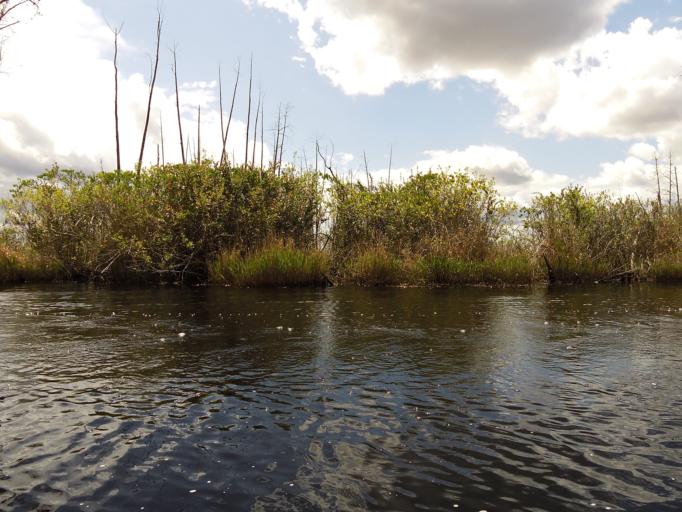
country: US
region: Georgia
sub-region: Charlton County
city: Folkston
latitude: 30.7359
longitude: -82.1617
